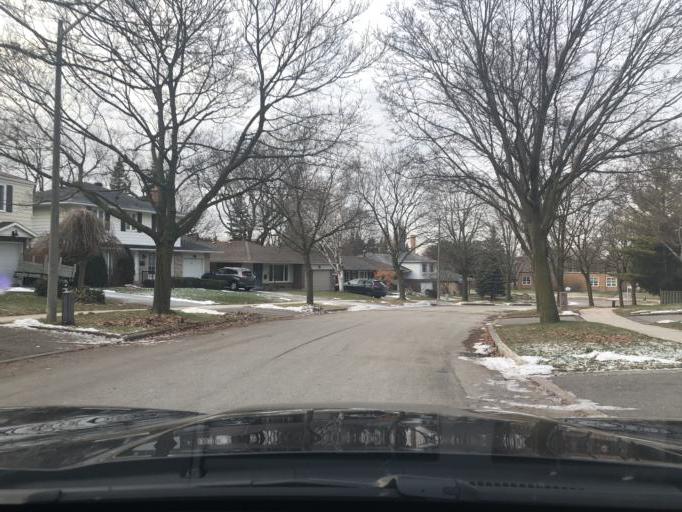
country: CA
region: Ontario
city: Willowdale
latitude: 43.7711
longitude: -79.3500
